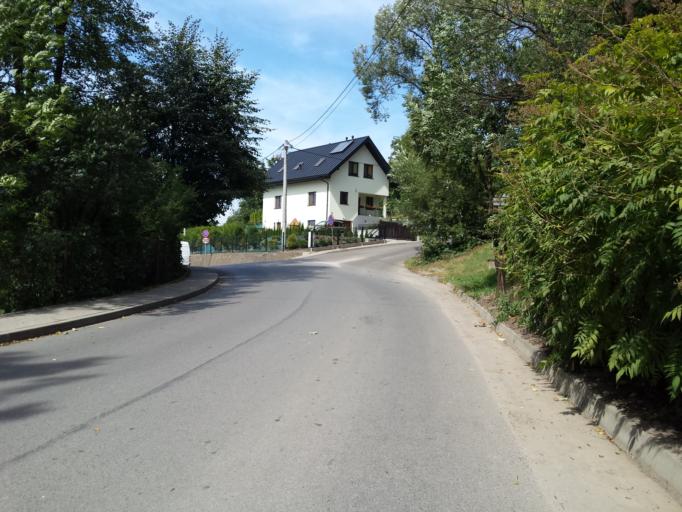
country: PL
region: Subcarpathian Voivodeship
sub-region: Powiat leski
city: Lesko
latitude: 49.4730
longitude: 22.3316
